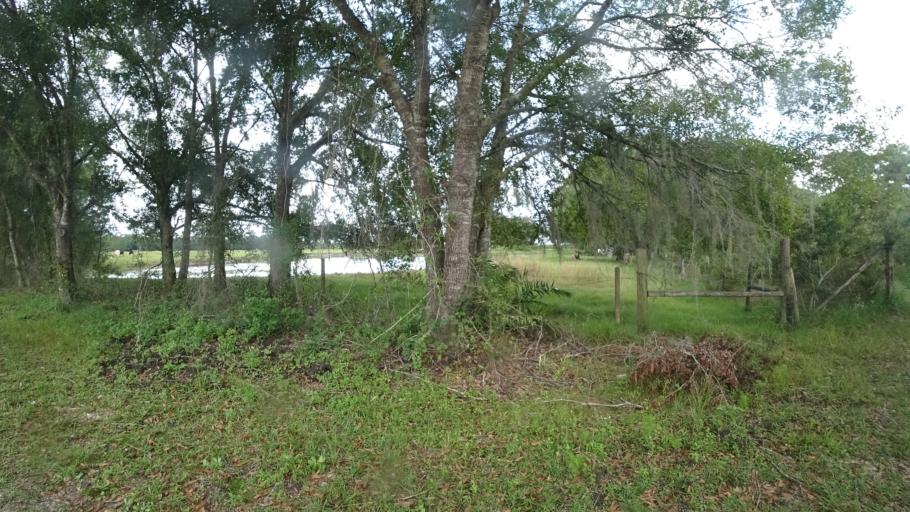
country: US
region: Florida
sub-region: Sarasota County
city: Lake Sarasota
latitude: 27.3937
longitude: -82.2664
